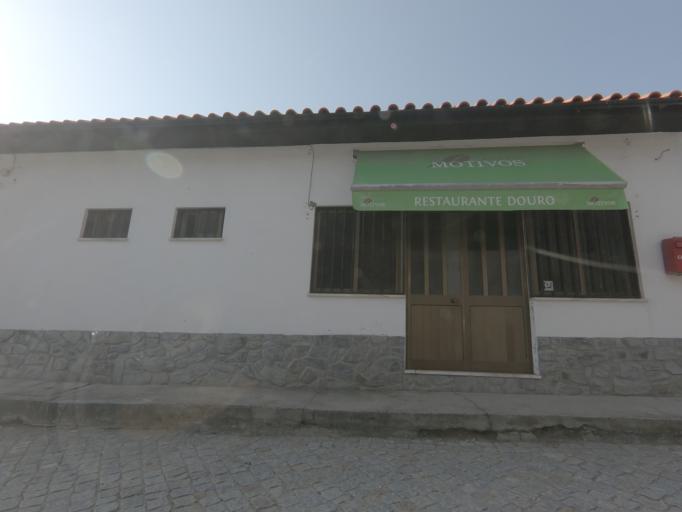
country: PT
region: Viseu
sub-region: Tabuaco
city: Tabuaco
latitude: 41.1585
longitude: -7.5535
